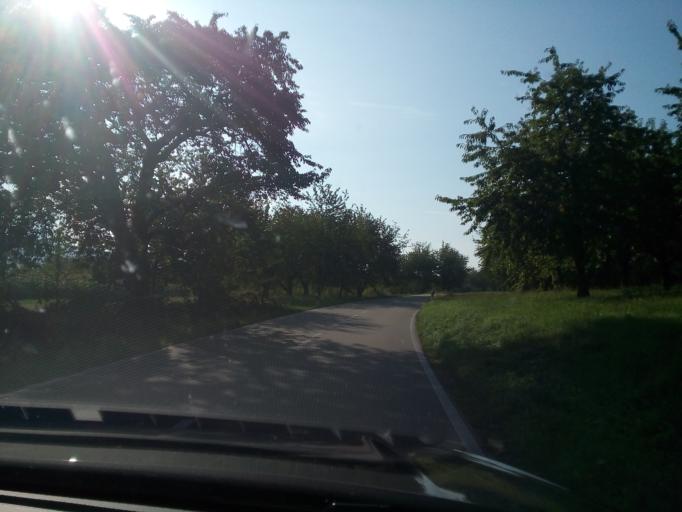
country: DE
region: Baden-Wuerttemberg
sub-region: Freiburg Region
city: Haslach
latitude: 48.5596
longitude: 8.0480
